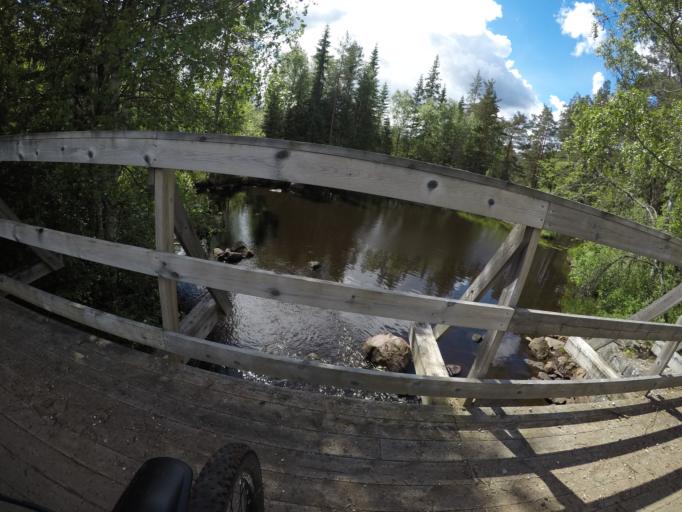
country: SE
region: Vaermland
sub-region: Filipstads Kommun
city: Lesjofors
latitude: 60.1359
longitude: 14.3203
